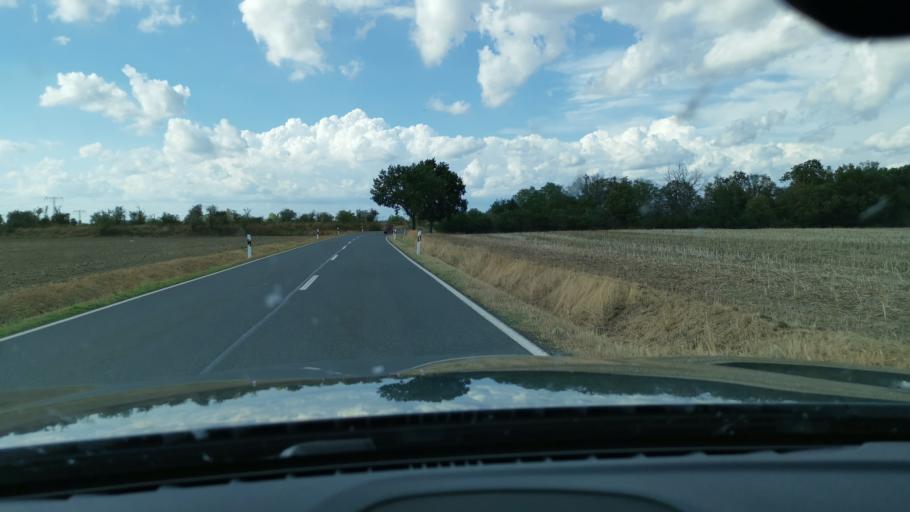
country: DE
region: Saxony
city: Zschepplin
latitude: 51.4893
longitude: 12.6011
